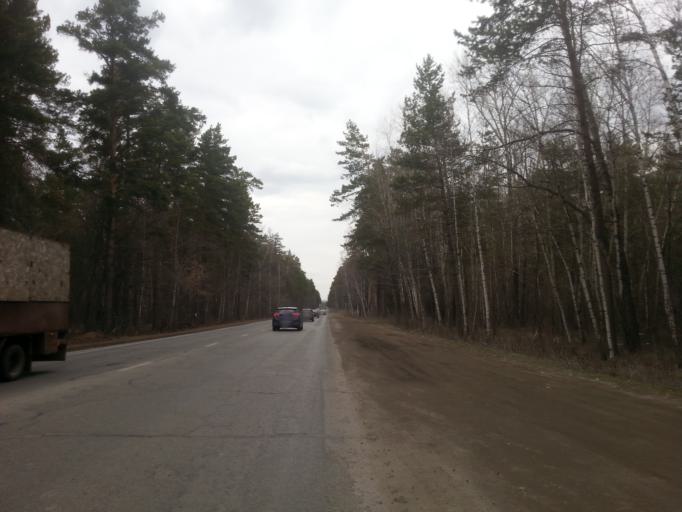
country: RU
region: Altai Krai
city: Yuzhnyy
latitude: 53.2756
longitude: 83.7208
